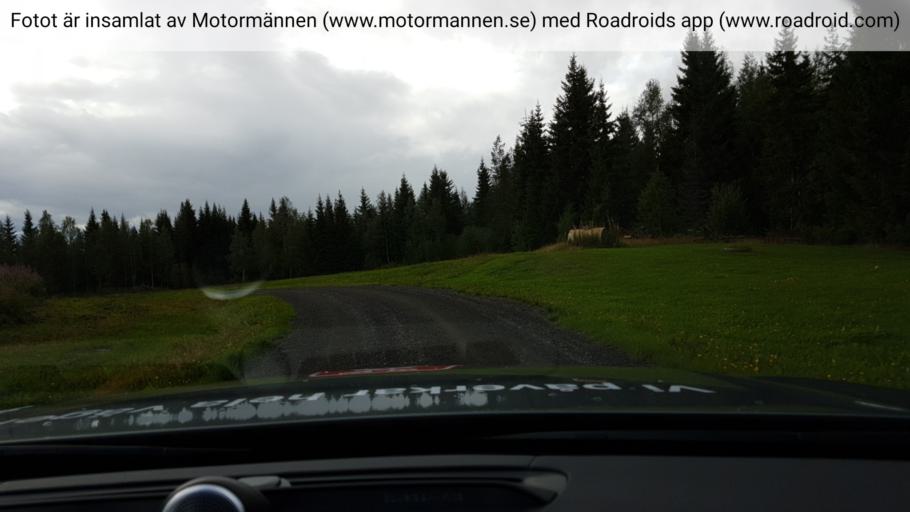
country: SE
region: Jaemtland
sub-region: Krokoms Kommun
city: Krokom
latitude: 63.7761
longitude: 14.6388
